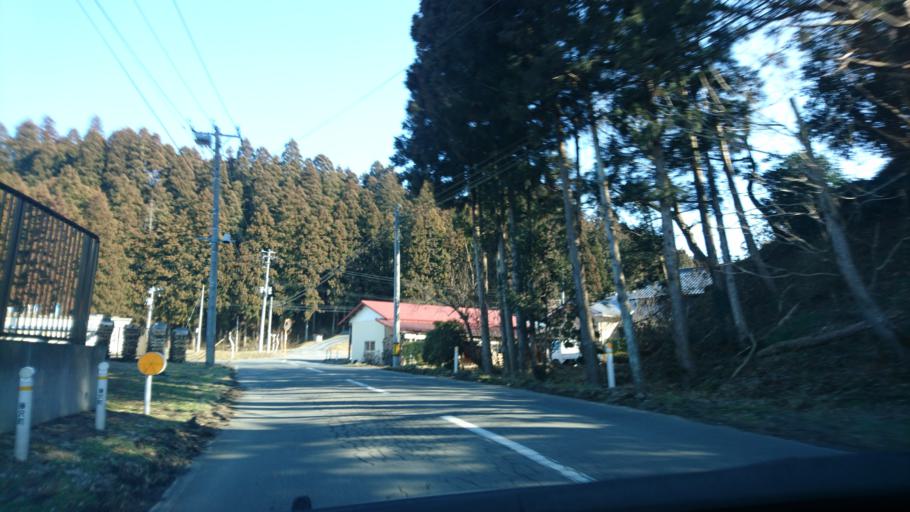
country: JP
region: Iwate
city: Ichinoseki
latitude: 38.8454
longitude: 141.2951
